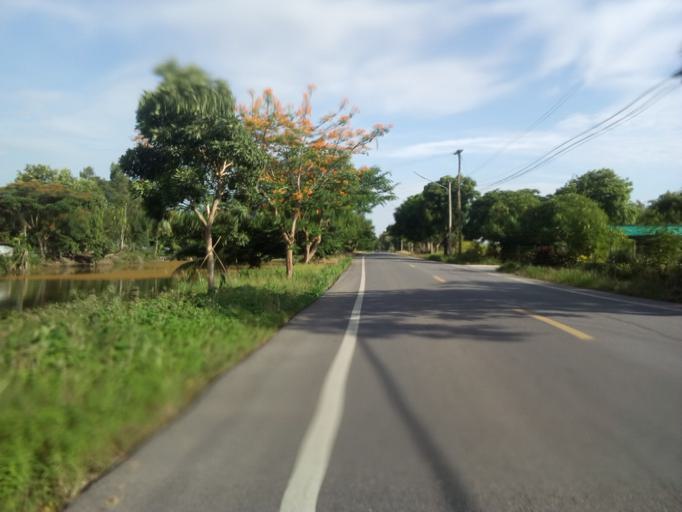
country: TH
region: Pathum Thani
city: Nong Suea
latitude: 14.1195
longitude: 100.8460
